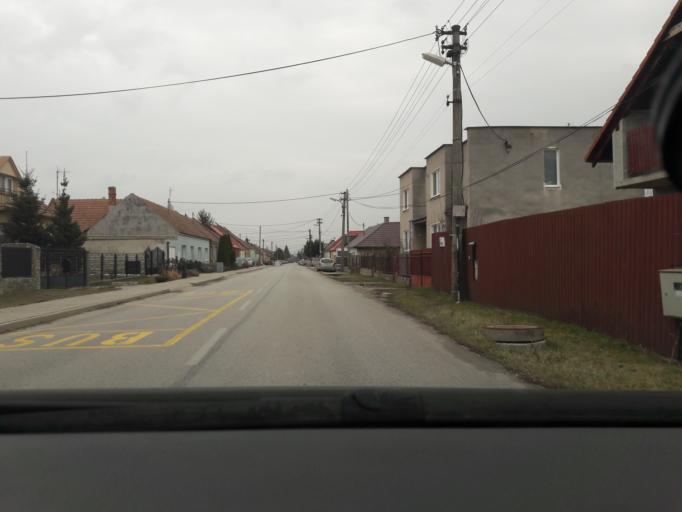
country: SK
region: Bratislavsky
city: Senec
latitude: 48.3146
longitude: 17.4401
